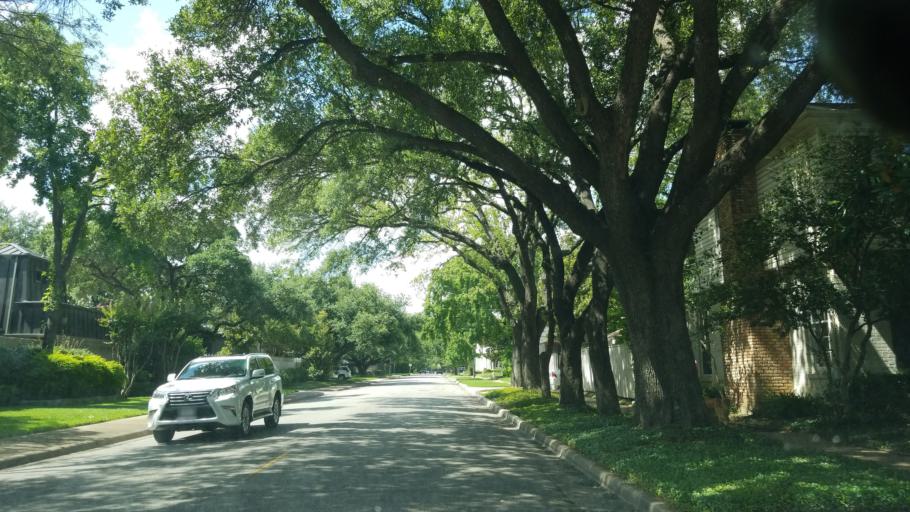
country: US
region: Texas
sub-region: Dallas County
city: University Park
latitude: 32.8304
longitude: -96.8191
